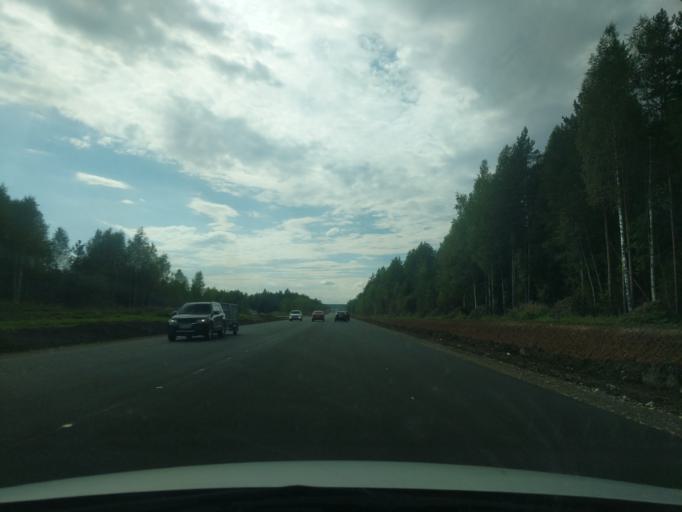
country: RU
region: Kostroma
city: Sudislavl'
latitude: 57.8231
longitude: 41.4951
